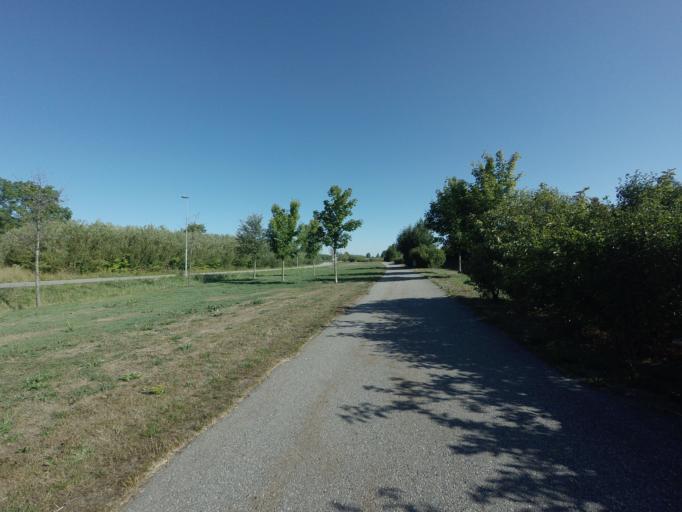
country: SE
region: Skane
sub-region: Trelleborgs Kommun
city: Skare
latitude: 55.4068
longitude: 13.0714
